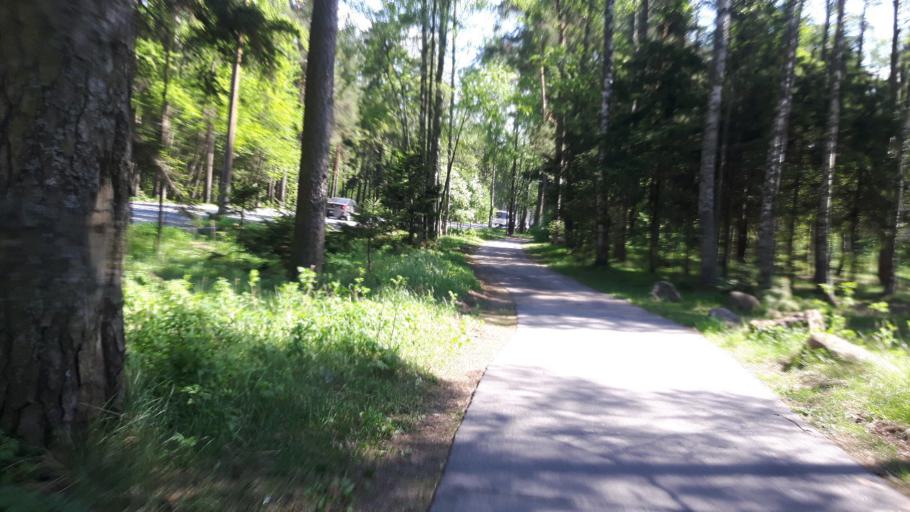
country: RU
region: St.-Petersburg
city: Komarovo
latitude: 60.1717
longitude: 29.8104
